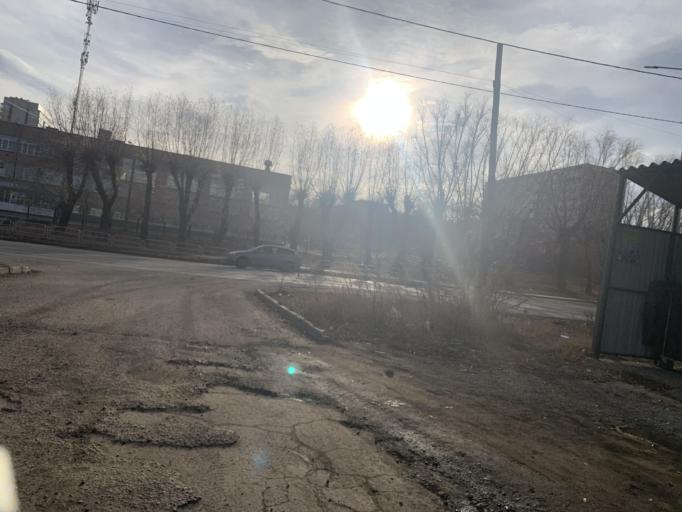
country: RU
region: Chelyabinsk
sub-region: Gorod Chelyabinsk
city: Chelyabinsk
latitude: 55.1988
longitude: 61.3413
